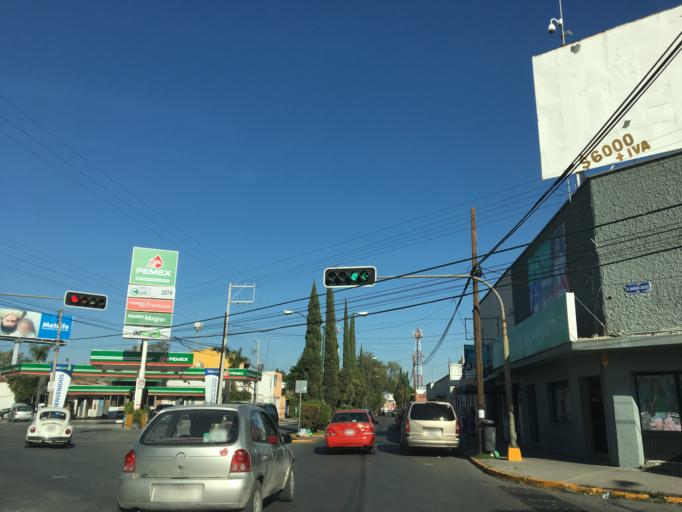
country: MX
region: San Luis Potosi
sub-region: San Luis Potosi
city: San Luis Potosi
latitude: 22.1472
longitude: -100.9839
